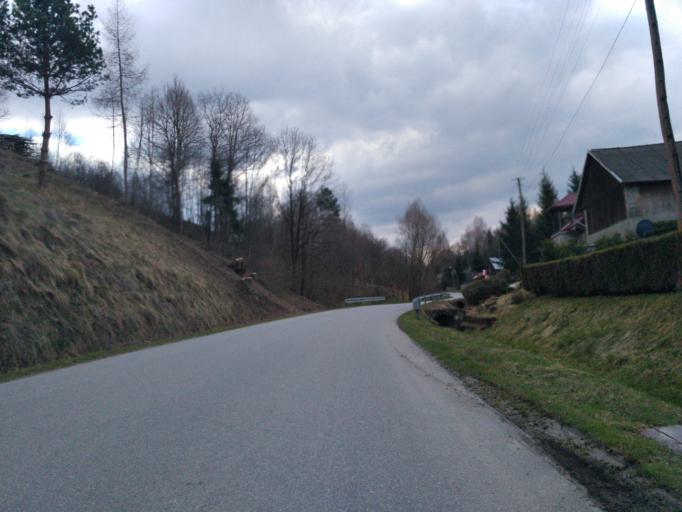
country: PL
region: Subcarpathian Voivodeship
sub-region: Powiat brzozowski
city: Dydnia
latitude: 49.6672
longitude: 22.1920
